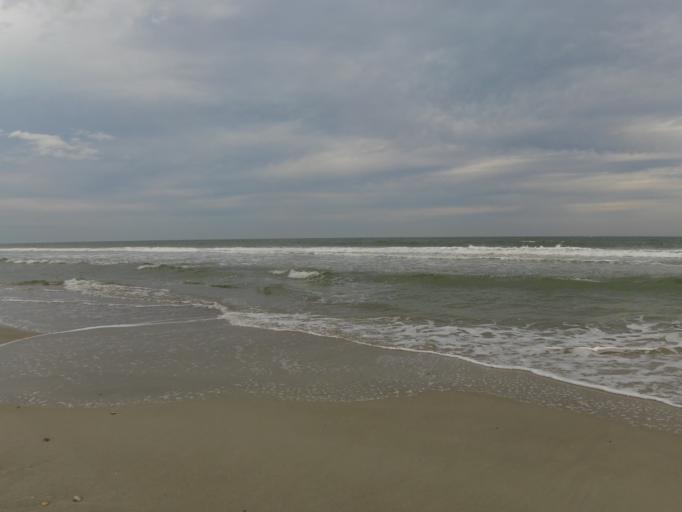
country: US
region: Florida
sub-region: Duval County
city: Neptune Beach
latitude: 30.3199
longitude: -81.3935
